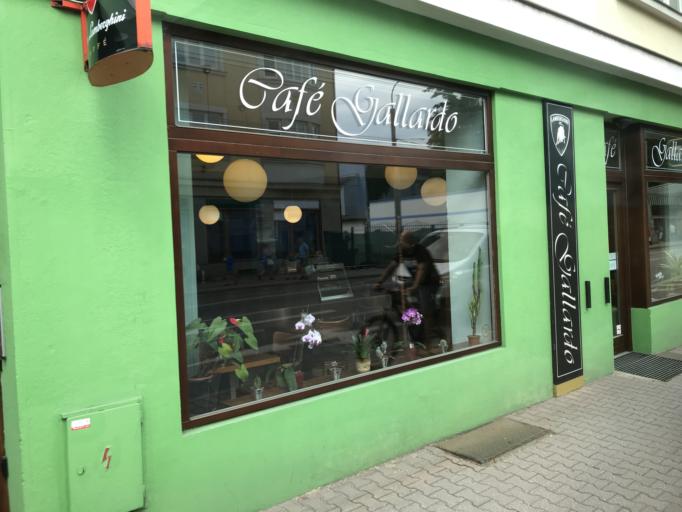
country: CZ
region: Jihocesky
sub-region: Okres Ceske Budejovice
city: Ceske Budejovice
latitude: 48.9663
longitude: 14.4749
